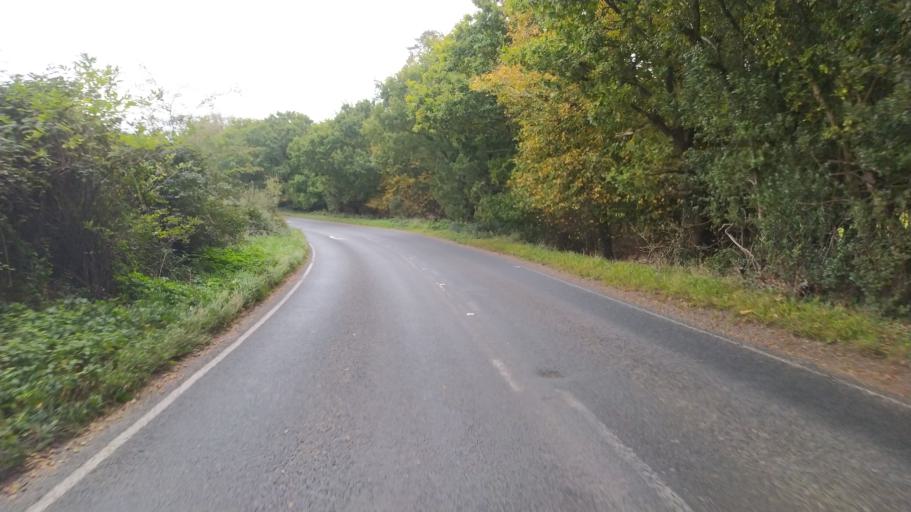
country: GB
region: England
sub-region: Hampshire
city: Lymington
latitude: 50.7792
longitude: -1.5561
